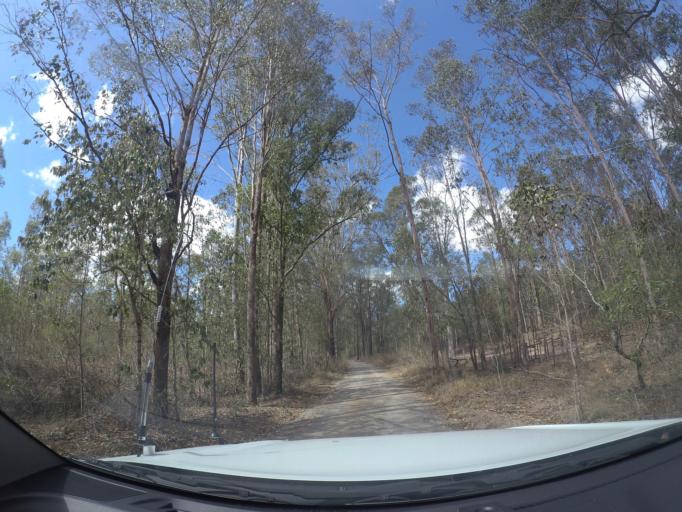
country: AU
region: Queensland
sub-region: Logan
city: North Maclean
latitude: -27.8305
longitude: 152.9677
